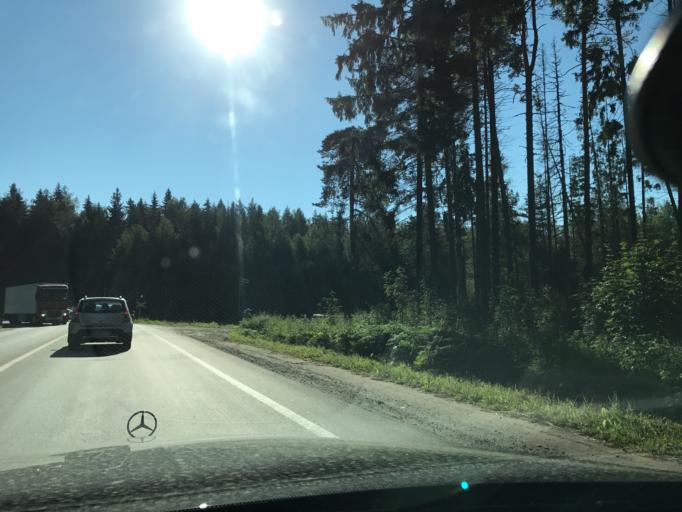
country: RU
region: Moskovskaya
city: Chernogolovka
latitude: 55.9843
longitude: 38.3479
